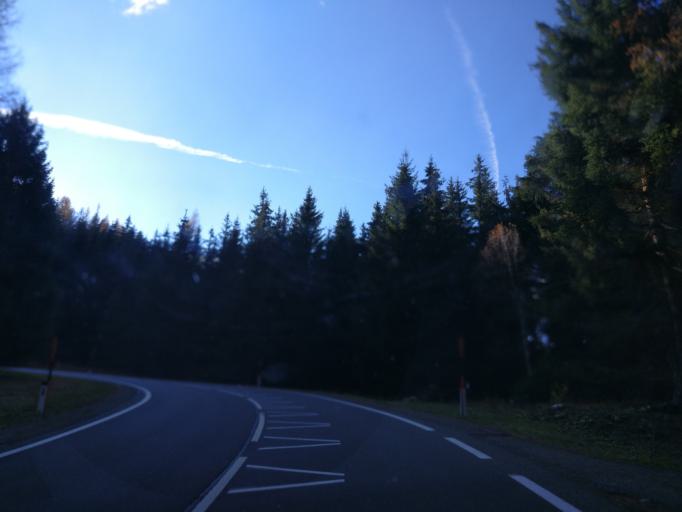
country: AT
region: Salzburg
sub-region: Politischer Bezirk Zell am See
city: Dienten am Hochkonig
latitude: 47.4045
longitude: 12.9840
